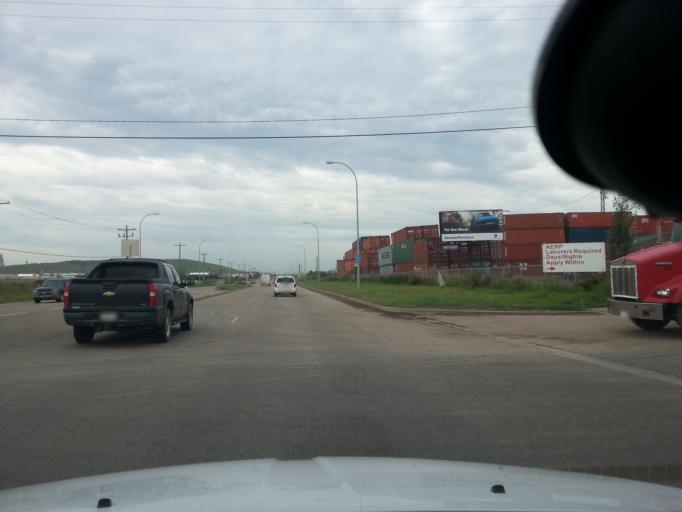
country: CA
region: Alberta
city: St. Albert
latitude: 53.5968
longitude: -113.6152
